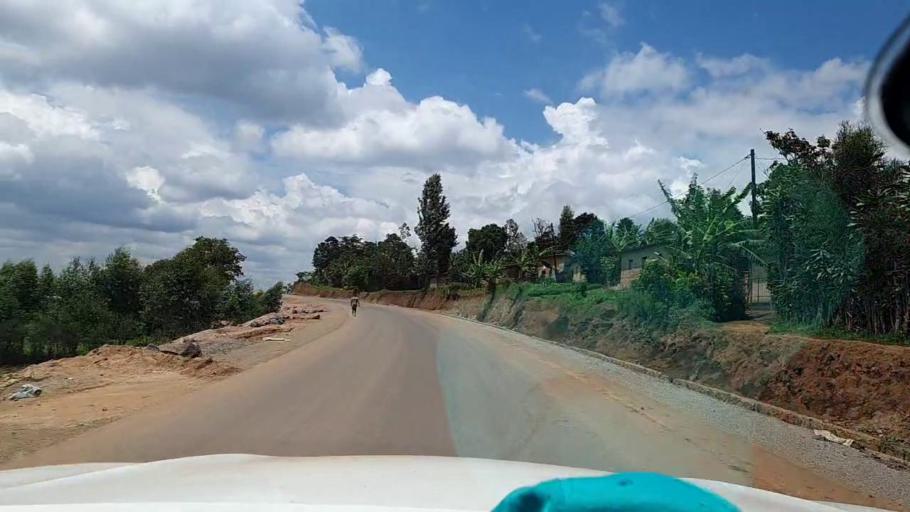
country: RW
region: Southern Province
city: Nzega
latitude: -2.6460
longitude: 29.5700
